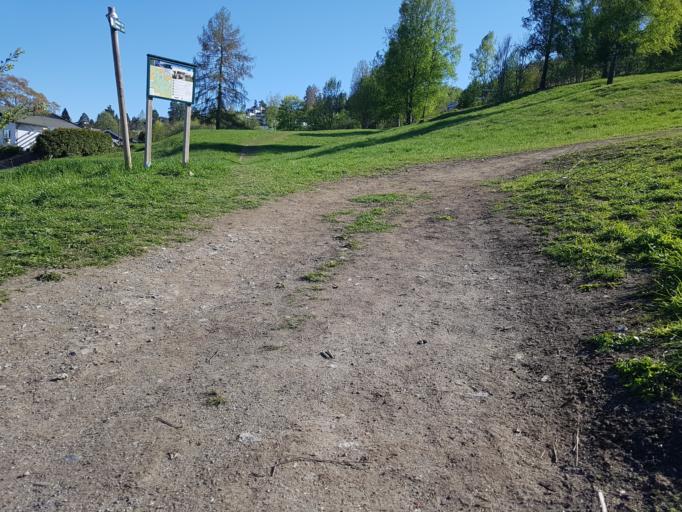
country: NO
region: Buskerud
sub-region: Drammen
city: Drammen
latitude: 59.7279
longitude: 10.2018
